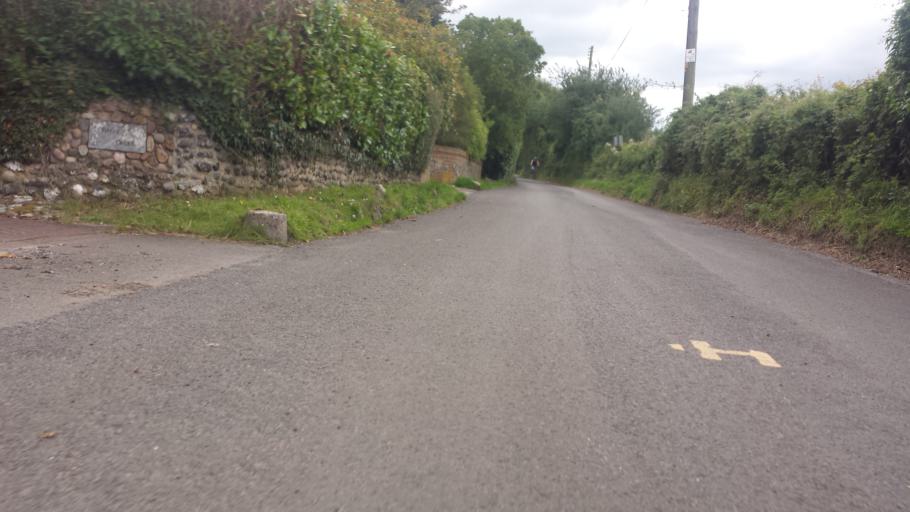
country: GB
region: England
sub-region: Kent
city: Swanley
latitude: 51.3768
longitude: 0.1597
